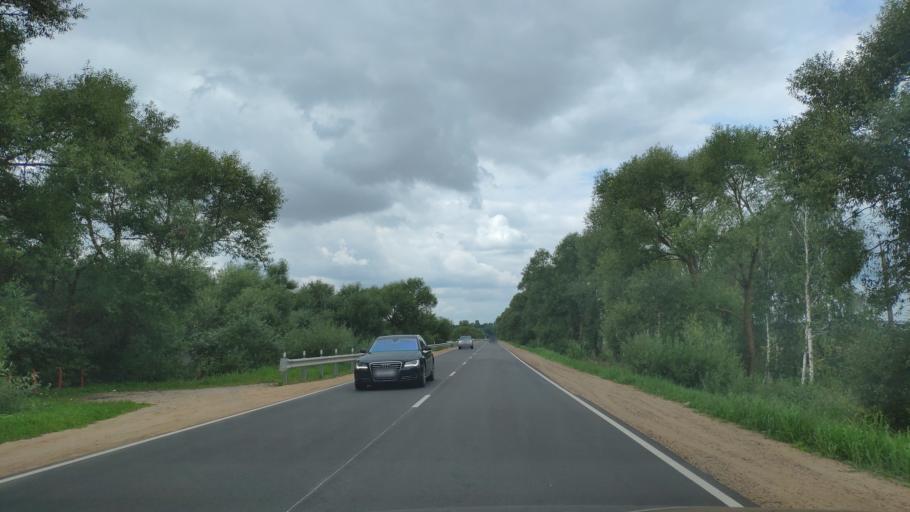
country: BY
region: Minsk
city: Syomkava
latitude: 53.9951
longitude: 27.4629
